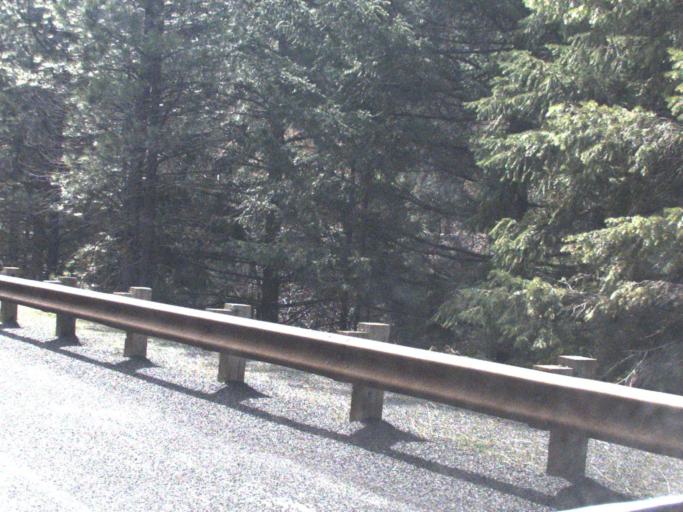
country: US
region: Washington
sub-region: Kittitas County
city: Cle Elum
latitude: 46.9479
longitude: -121.0707
